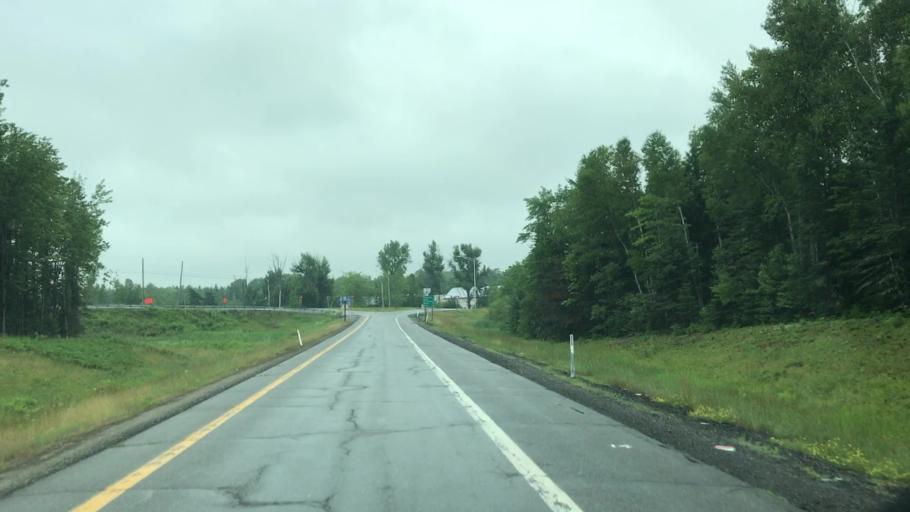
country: US
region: Maine
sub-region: Penobscot County
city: Howland
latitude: 45.2350
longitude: -68.6759
